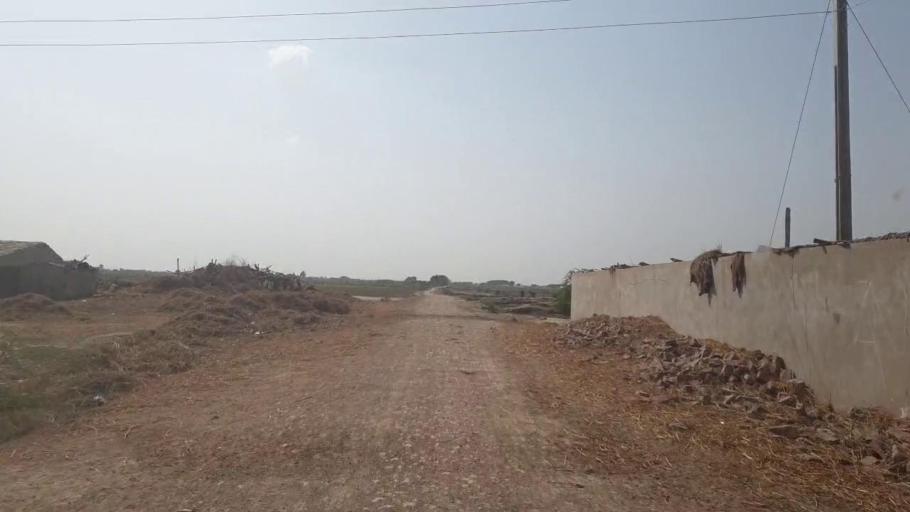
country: PK
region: Sindh
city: Jati
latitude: 24.5150
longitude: 68.5233
